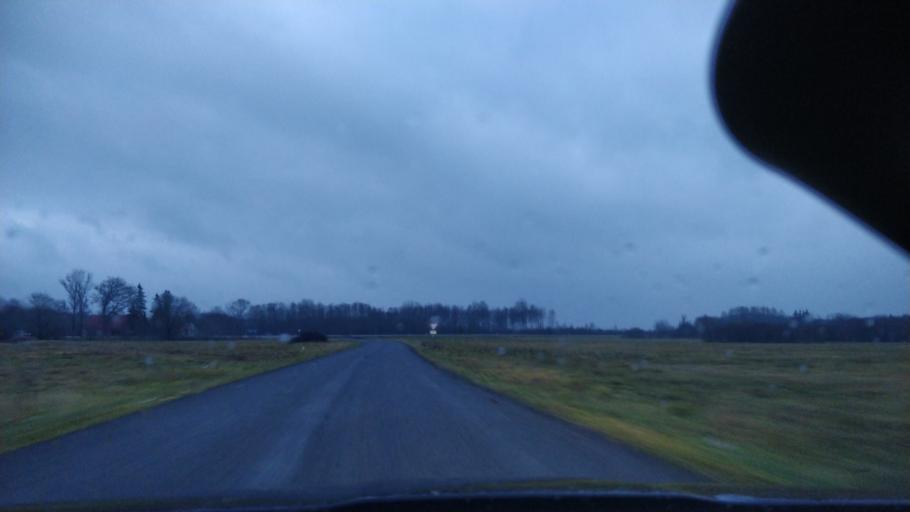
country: EE
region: Laeaene
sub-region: Lihula vald
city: Lihula
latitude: 58.8363
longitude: 24.0513
